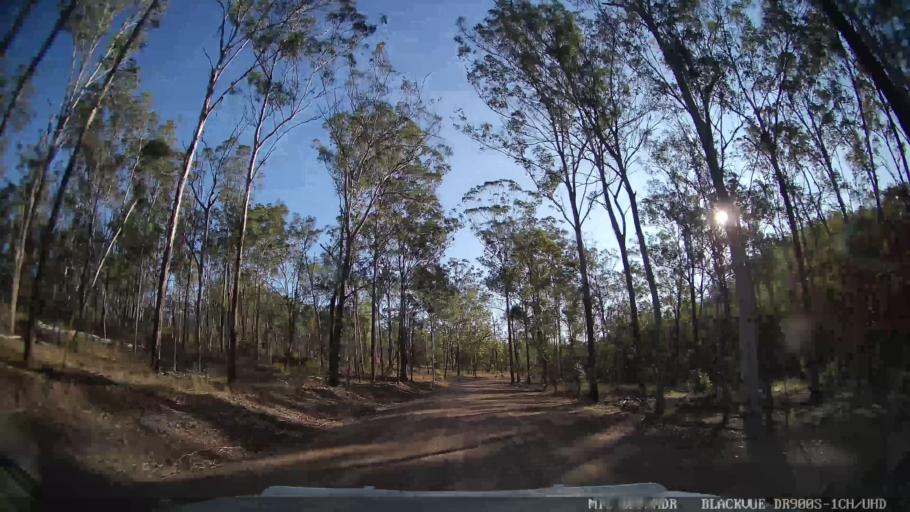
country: AU
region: Queensland
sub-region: Gladstone
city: Toolooa
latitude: -24.6953
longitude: 151.4089
